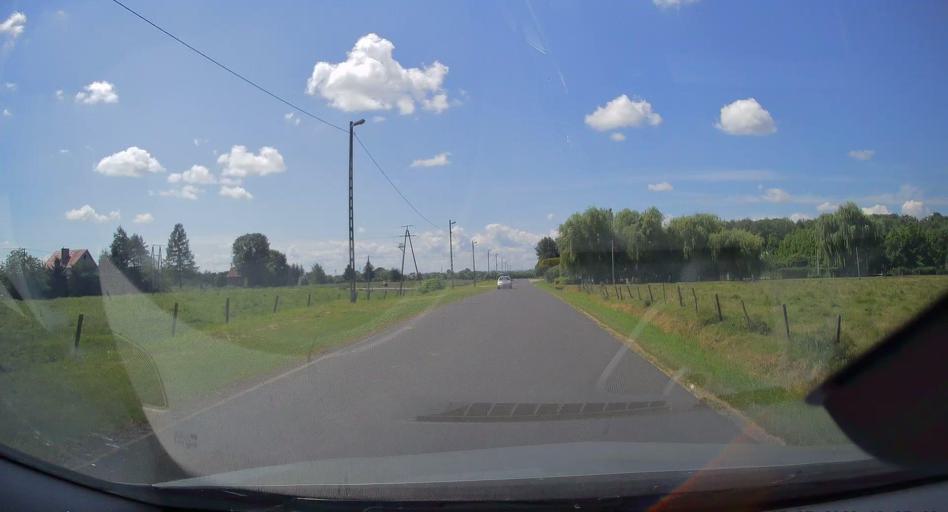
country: PL
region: Subcarpathian Voivodeship
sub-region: Powiat przemyski
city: Medyka
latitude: 49.8192
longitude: 22.8646
